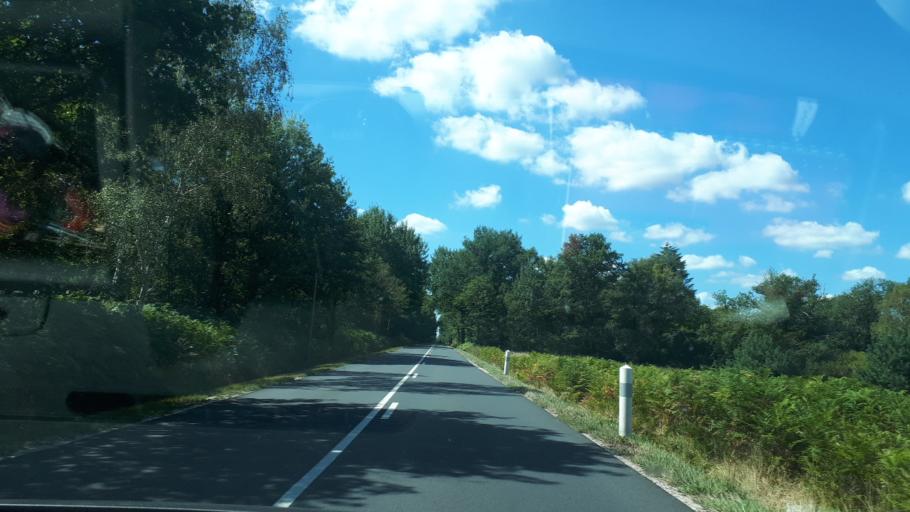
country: FR
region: Centre
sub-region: Departement du Loir-et-Cher
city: Chaumont-sur-Tharonne
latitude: 47.5754
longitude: 1.9241
